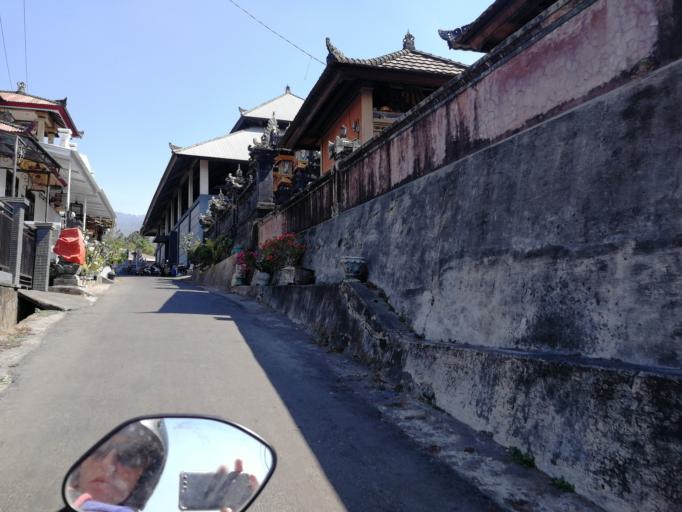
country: ID
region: Bali
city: Banjar Kedisan
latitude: -8.1499
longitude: 115.3065
